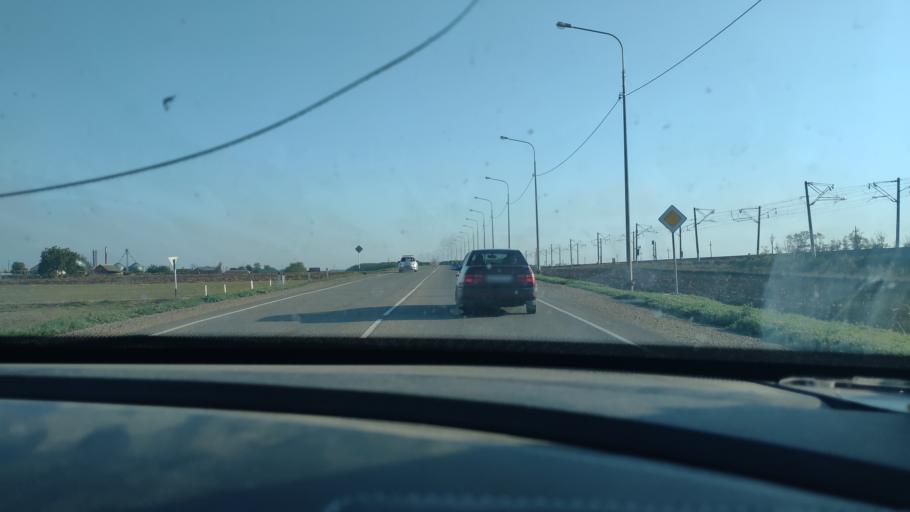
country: RU
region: Krasnodarskiy
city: Novominskaya
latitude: 46.3113
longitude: 38.9307
